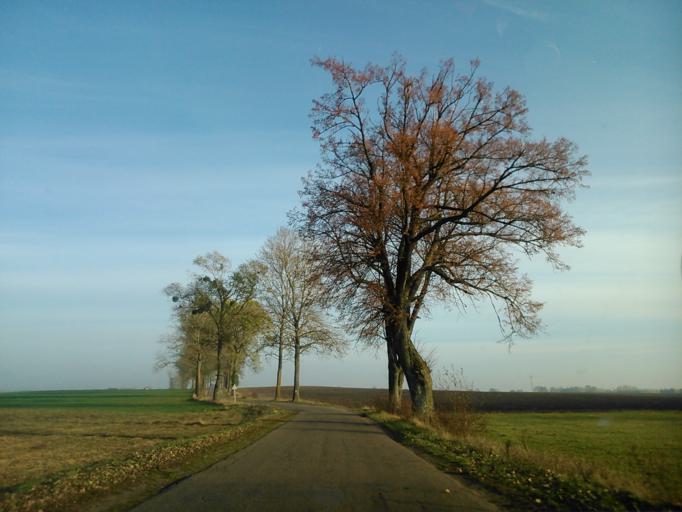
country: PL
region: Warmian-Masurian Voivodeship
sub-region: Powiat dzialdowski
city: Rybno
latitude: 53.2742
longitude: 19.9870
